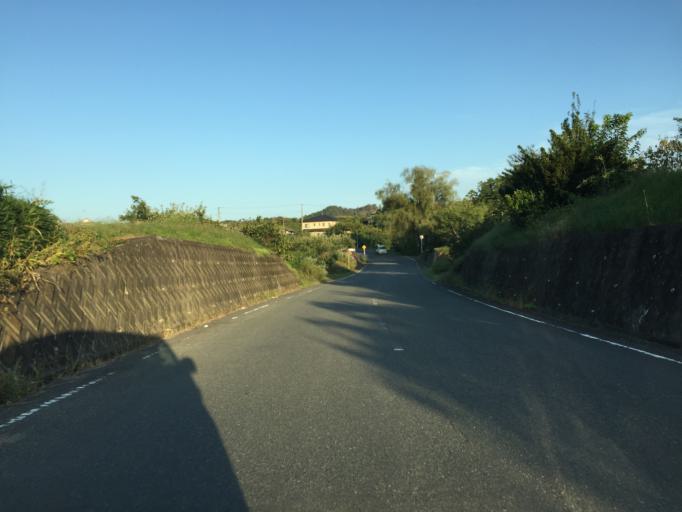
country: JP
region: Fukushima
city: Hobaramachi
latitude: 37.8035
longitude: 140.5674
